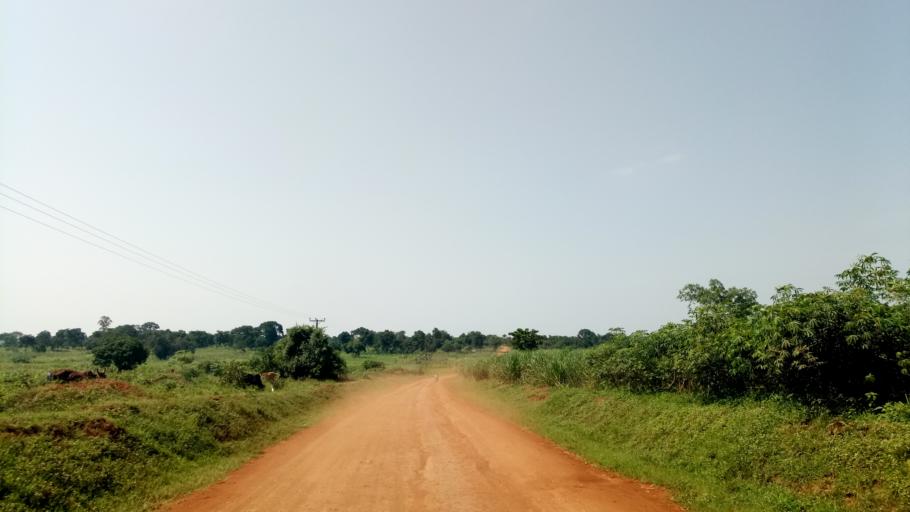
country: UG
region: Eastern Region
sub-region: Kaliro District
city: Kaliro
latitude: 0.9754
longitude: 33.4601
